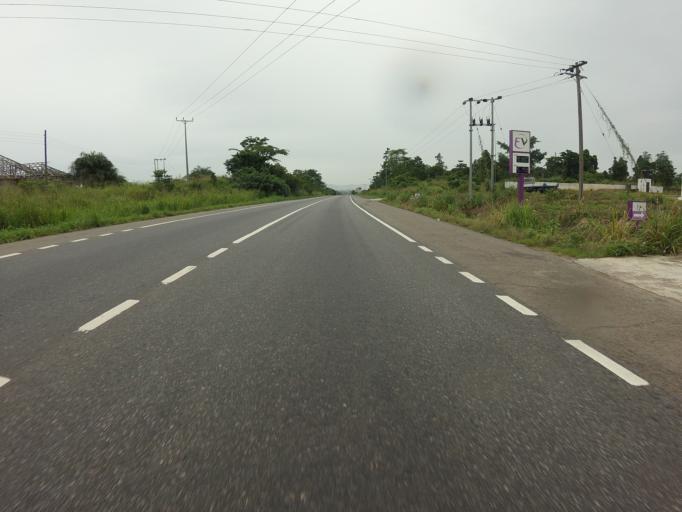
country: GH
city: Kibi
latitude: 6.1635
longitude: -0.4824
